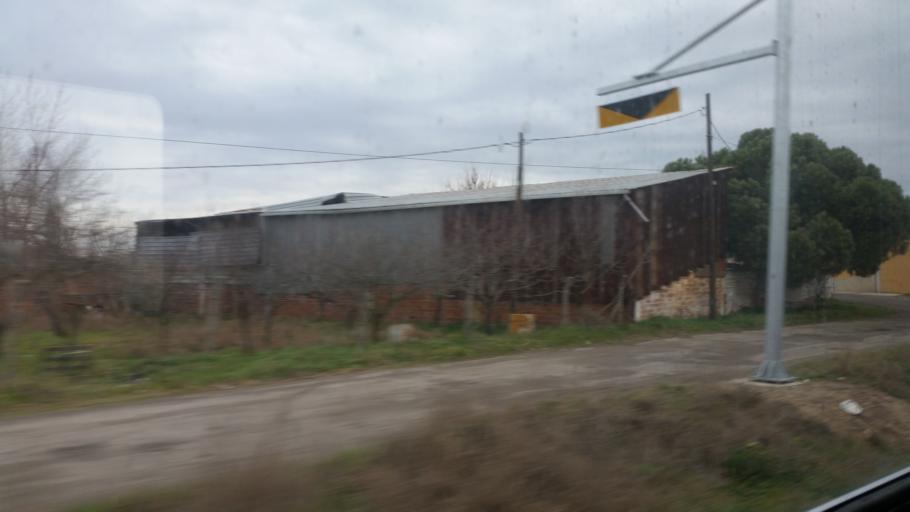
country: TR
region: Tekirdag
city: Corlu
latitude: 41.2074
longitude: 27.8316
